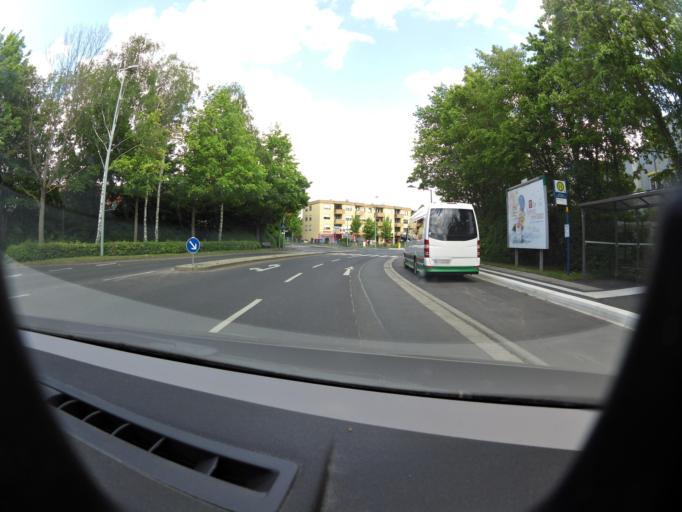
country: DE
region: Bavaria
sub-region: Regierungsbezirk Unterfranken
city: Kitzingen
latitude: 49.7422
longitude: 10.1498
